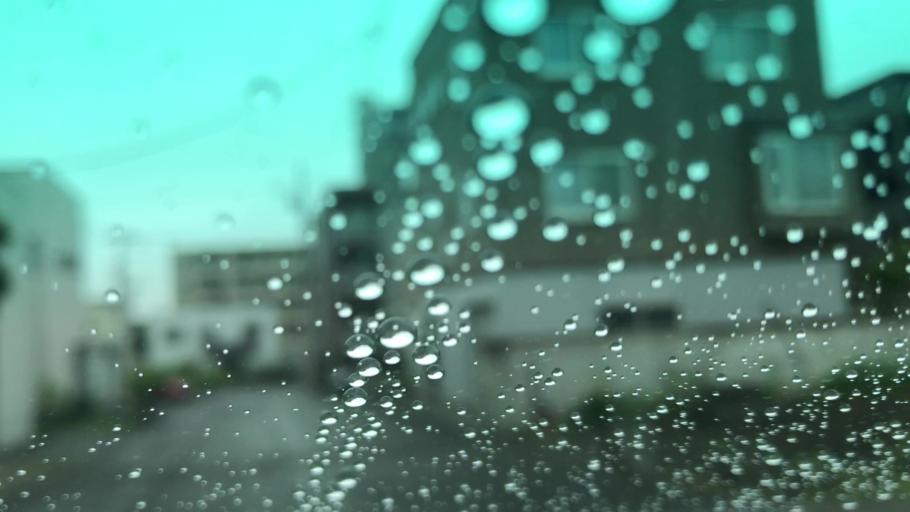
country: JP
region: Hokkaido
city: Sapporo
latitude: 43.0806
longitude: 141.2892
